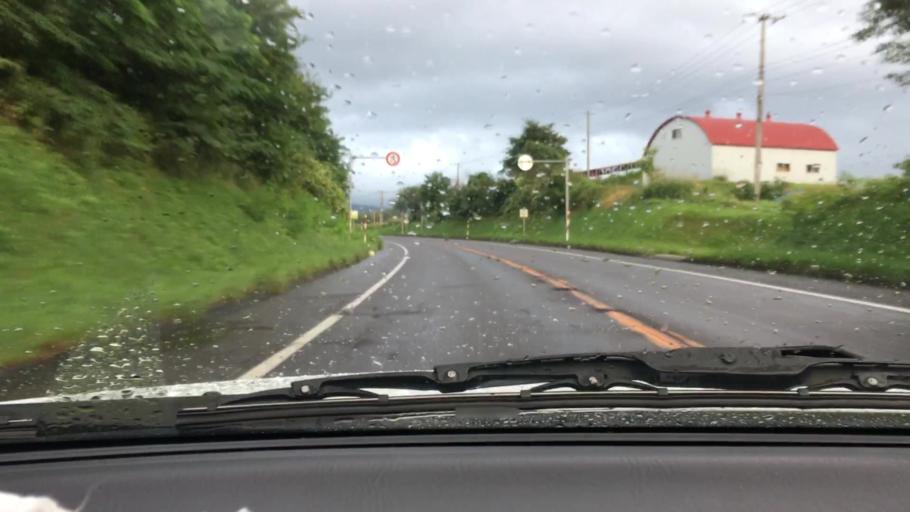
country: JP
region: Hokkaido
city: Nanae
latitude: 42.0816
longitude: 140.5885
